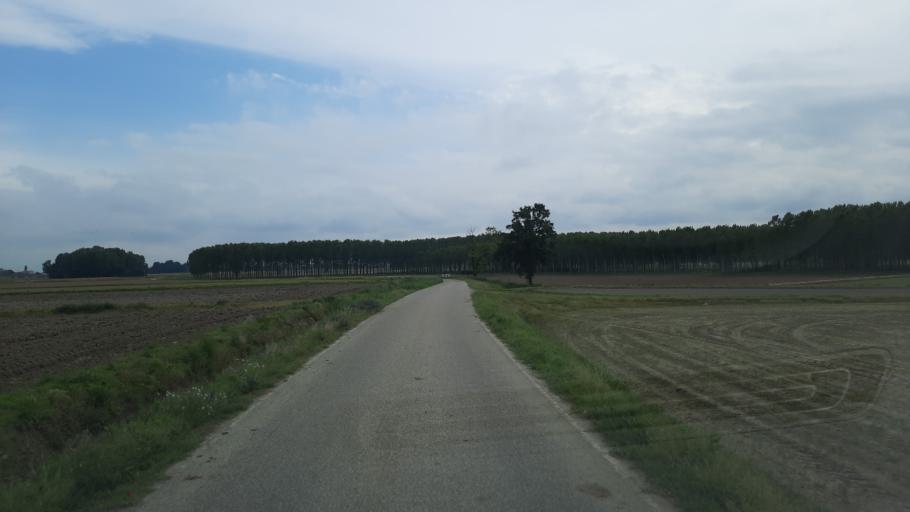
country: IT
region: Lombardy
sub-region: Provincia di Pavia
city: Cozzo
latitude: 45.2058
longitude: 8.6132
